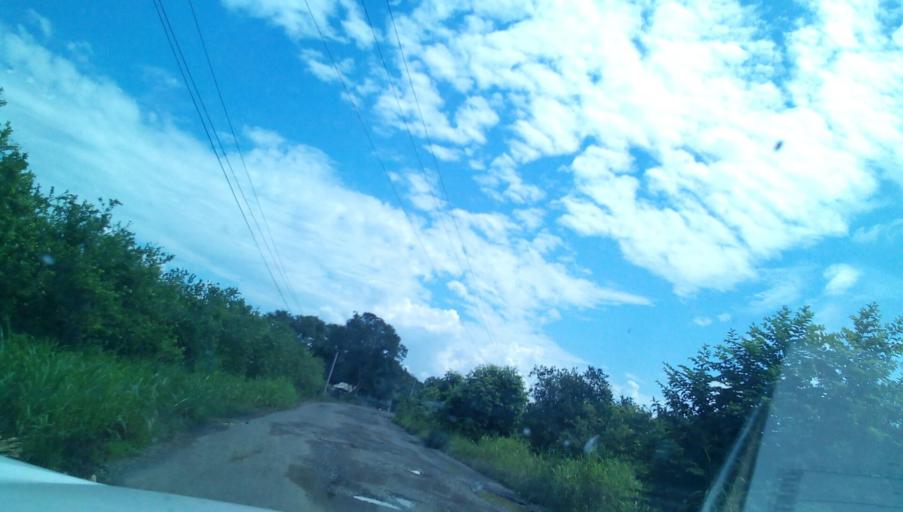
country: MX
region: Veracruz
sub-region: Alamo Temapache
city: Vegas de la Soledad y Soledad Dos
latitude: 20.9065
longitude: -97.9296
